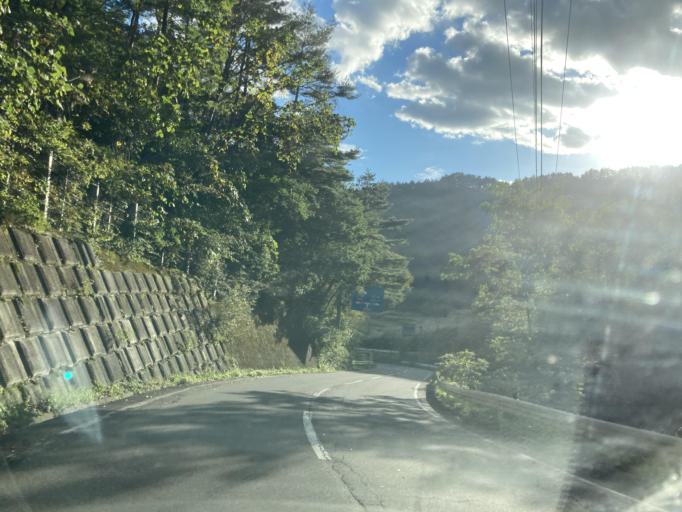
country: JP
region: Nagano
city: Ueda
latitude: 36.3948
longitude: 138.0981
